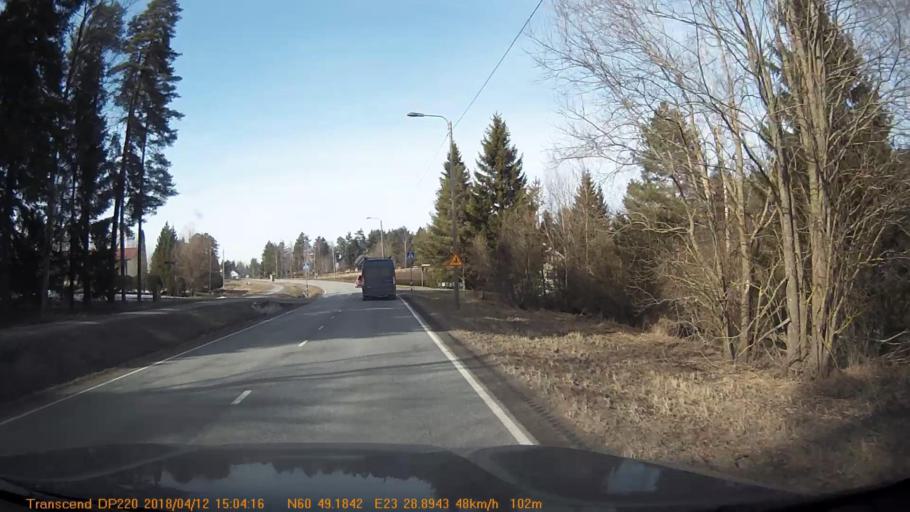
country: FI
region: Haeme
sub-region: Forssa
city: Jokioinen
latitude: 60.8199
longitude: 23.4815
